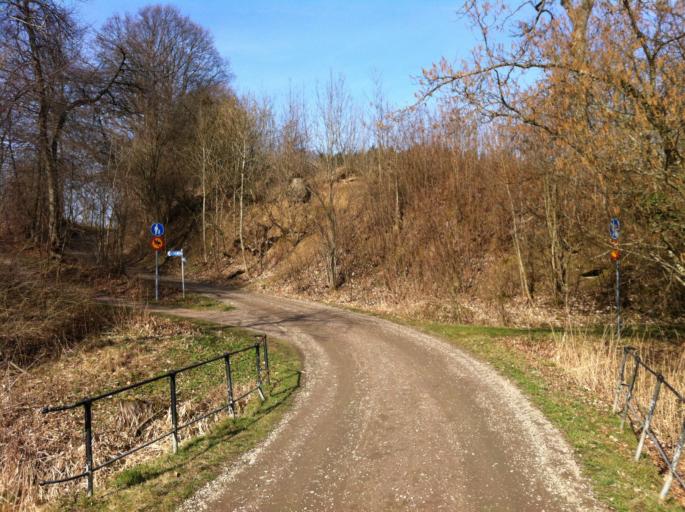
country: SE
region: Skane
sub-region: Helsingborg
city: Gantofta
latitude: 55.9995
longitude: 12.7863
